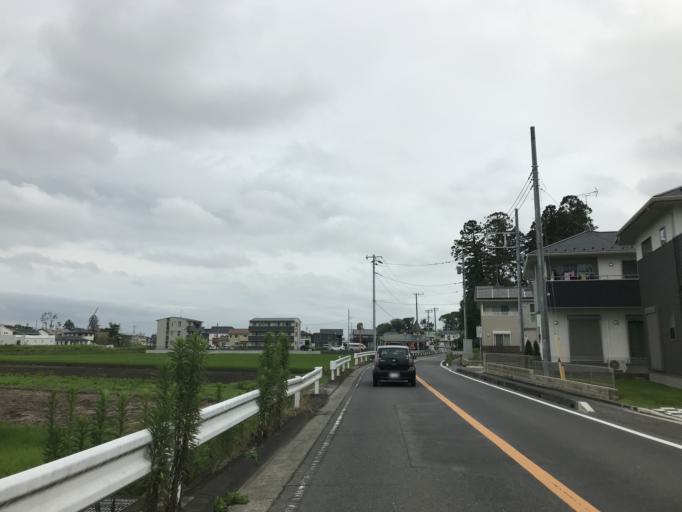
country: JP
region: Ibaraki
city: Mito-shi
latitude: 36.3336
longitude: 140.4578
